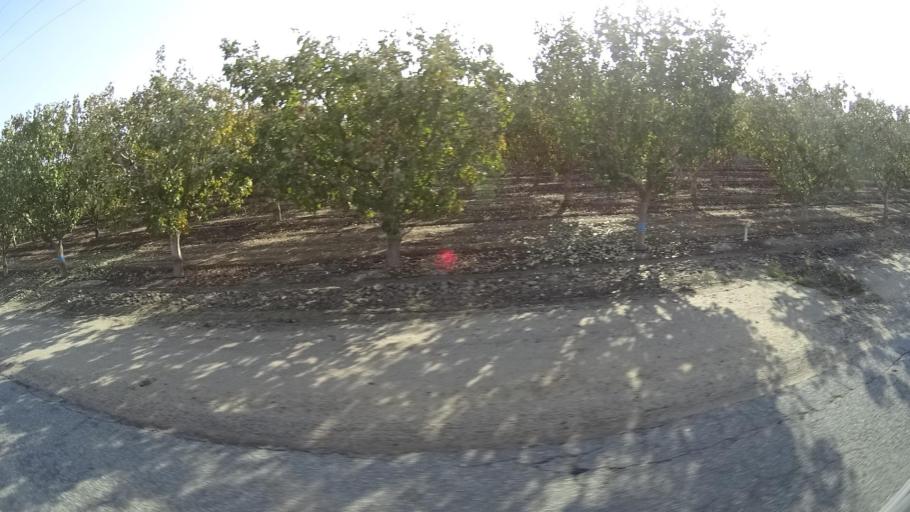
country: US
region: California
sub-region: Tulare County
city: Richgrove
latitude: 35.7908
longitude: -119.1084
